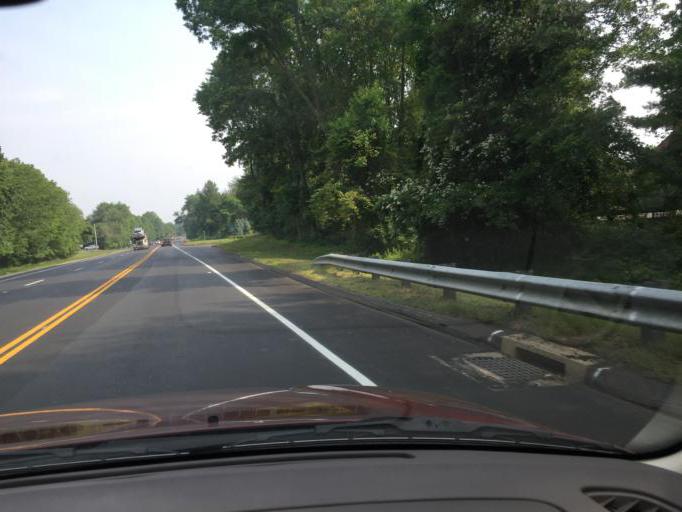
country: US
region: Connecticut
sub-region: Fairfield County
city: Westport
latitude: 41.1312
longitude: -73.3340
